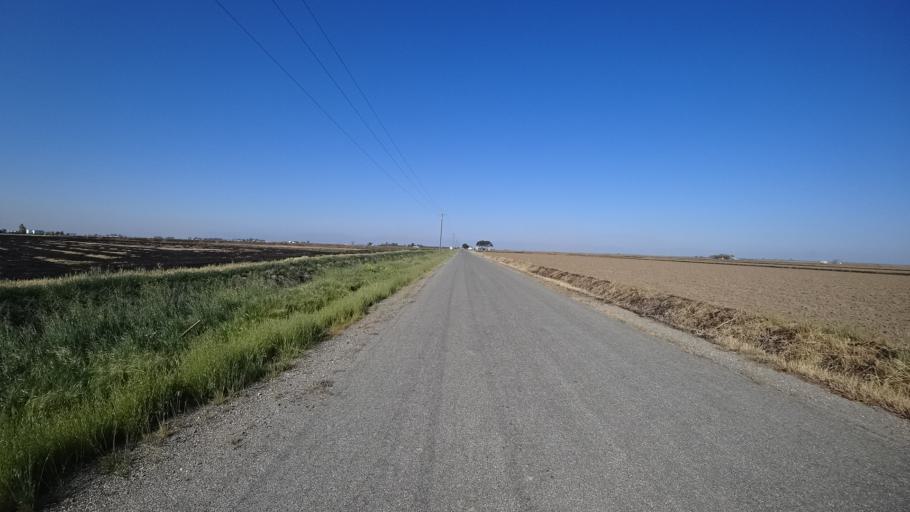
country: US
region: California
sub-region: Glenn County
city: Willows
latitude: 39.6016
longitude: -122.0656
